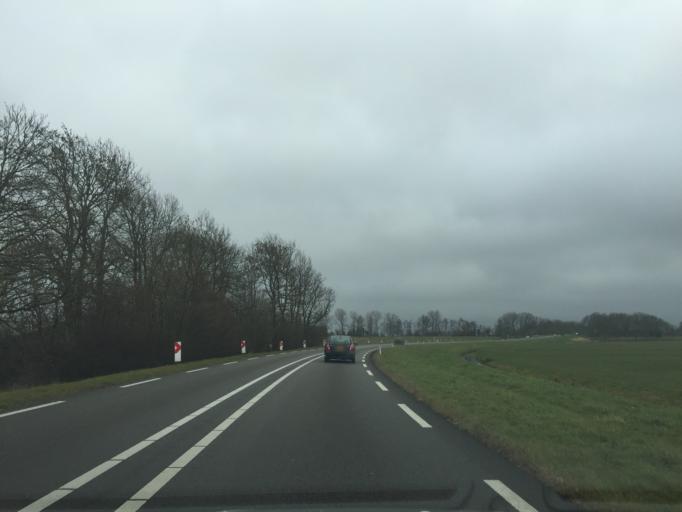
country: NL
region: South Holland
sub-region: Gemeente Kaag en Braassem
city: Leimuiden
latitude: 52.1957
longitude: 4.6803
